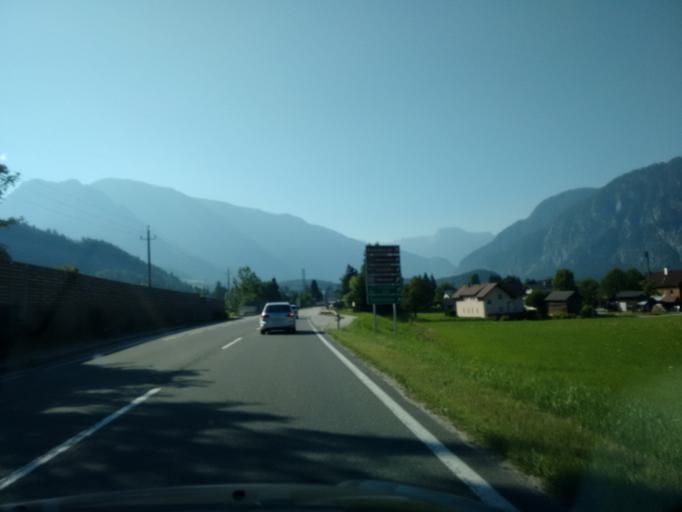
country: AT
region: Upper Austria
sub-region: Politischer Bezirk Gmunden
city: Bad Goisern
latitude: 47.6345
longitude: 13.6276
